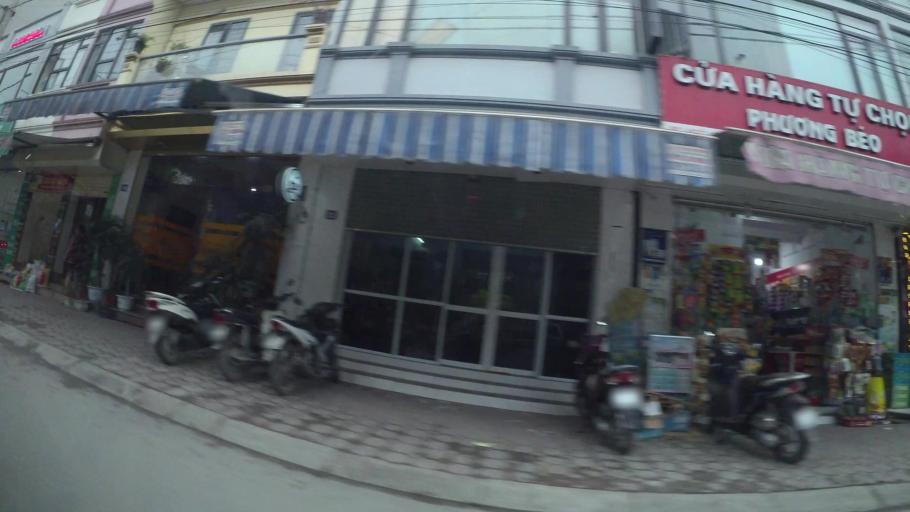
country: VN
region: Ha Noi
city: Hai BaTrung
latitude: 20.9900
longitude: 105.8726
